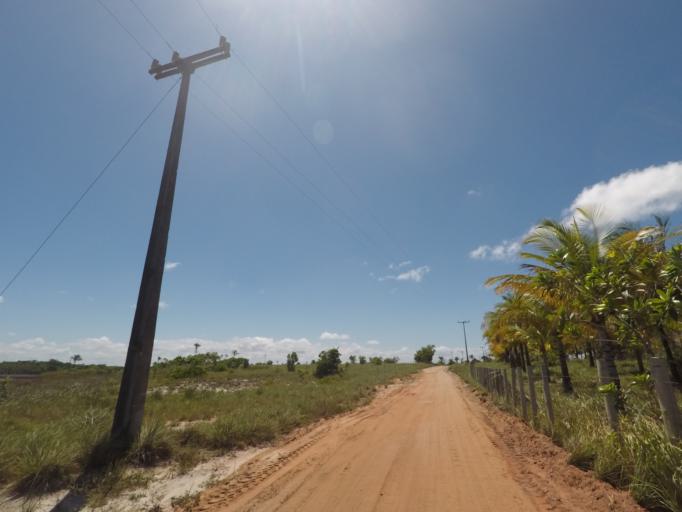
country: BR
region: Bahia
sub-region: Marau
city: Marau
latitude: -13.9680
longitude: -38.9428
